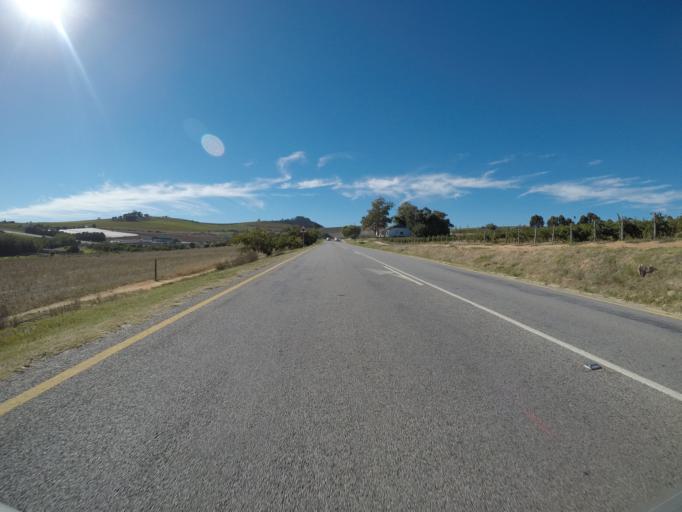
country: ZA
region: Western Cape
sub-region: City of Cape Town
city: Kraaifontein
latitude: -33.9656
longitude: 18.7447
